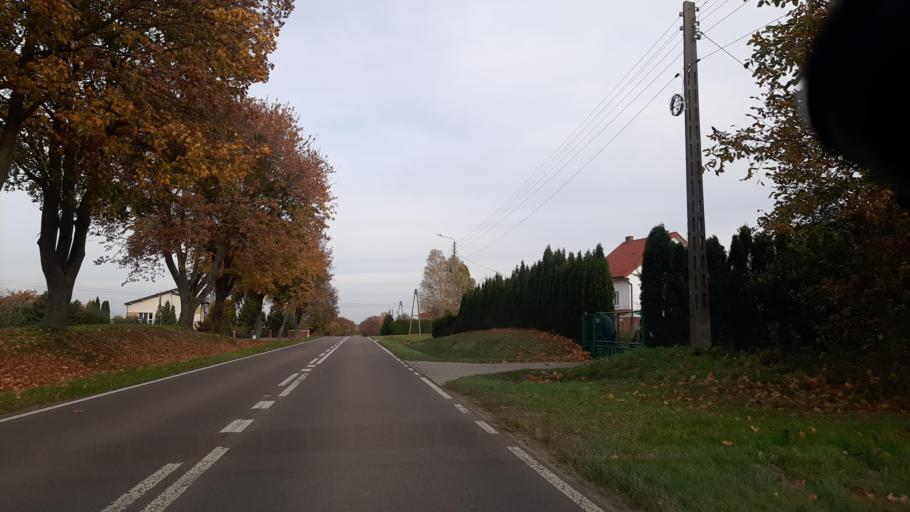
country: PL
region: Lublin Voivodeship
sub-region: Powiat pulawski
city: Markuszow
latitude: 51.3475
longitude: 22.2669
